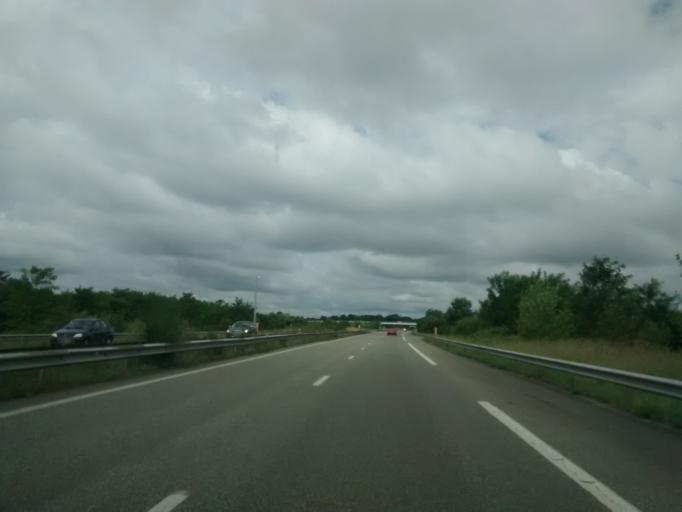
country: FR
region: Aquitaine
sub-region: Departement des Pyrenees-Atlantiques
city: Poey-de-Lescar
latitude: 43.3512
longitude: -0.4410
